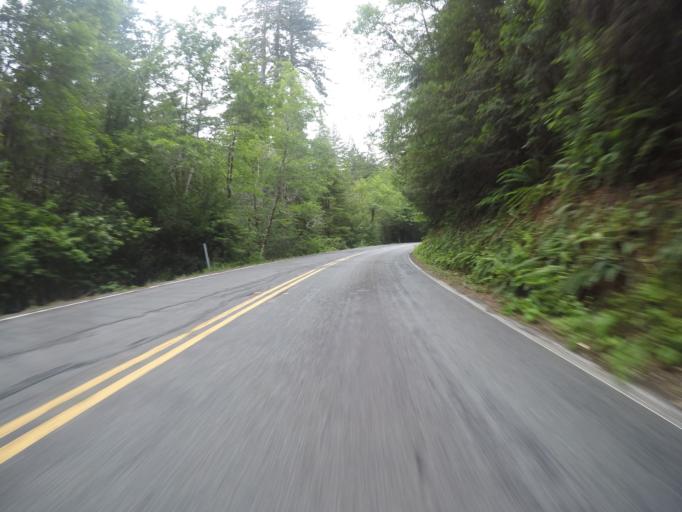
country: US
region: California
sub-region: Del Norte County
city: Bertsch-Oceanview
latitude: 41.7022
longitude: -123.9343
